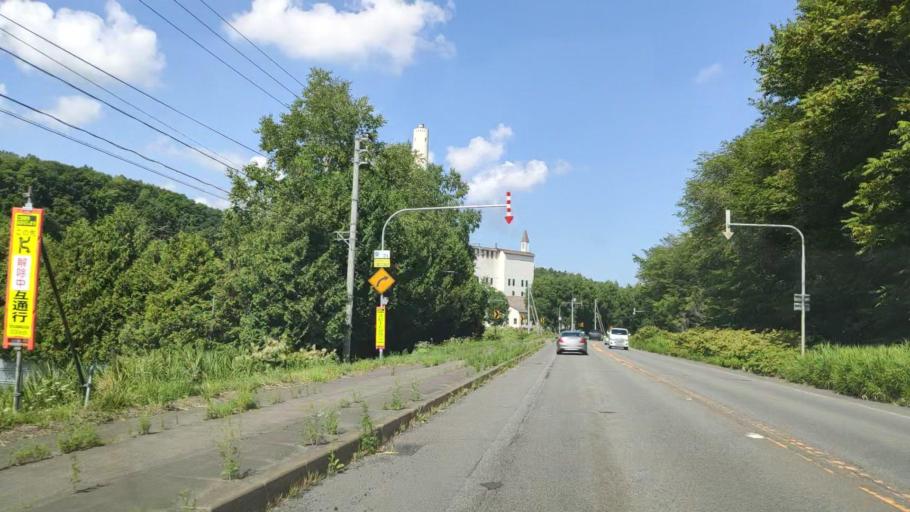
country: JP
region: Hokkaido
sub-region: Asahikawa-shi
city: Asahikawa
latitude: 43.6203
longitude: 142.4708
